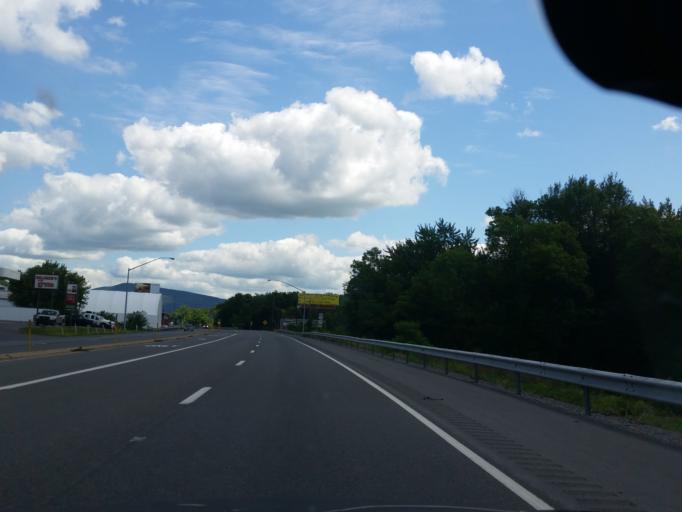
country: US
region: Pennsylvania
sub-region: Snyder County
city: Selinsgrove
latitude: 40.6929
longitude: -76.8780
